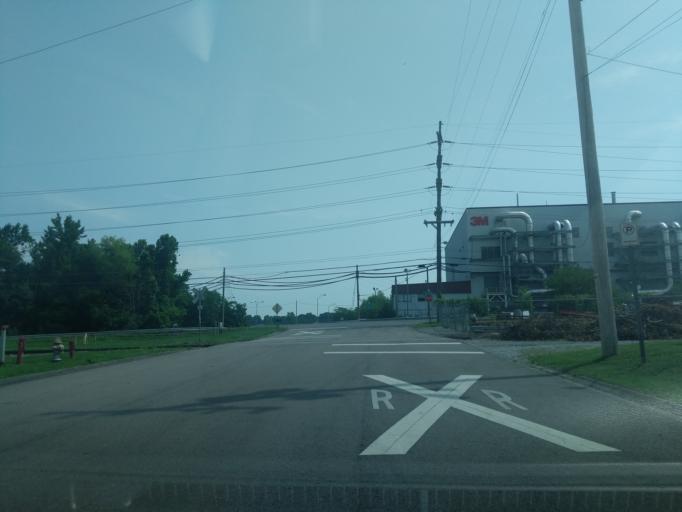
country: US
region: Tennessee
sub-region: Davidson County
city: Lakewood
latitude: 36.2734
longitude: -86.6657
